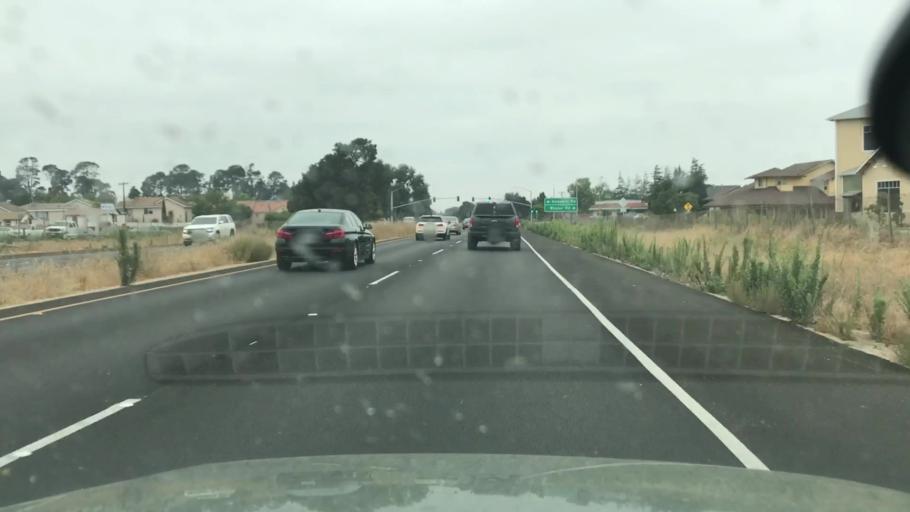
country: US
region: California
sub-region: Santa Barbara County
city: Orcutt
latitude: 34.8968
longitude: -120.4363
